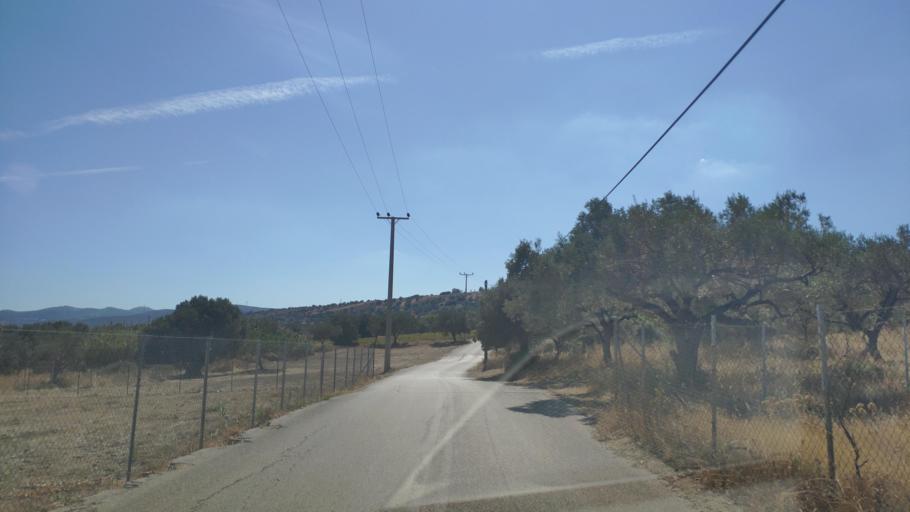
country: GR
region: Attica
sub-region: Nomarchia Anatolikis Attikis
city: Keratea
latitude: 37.8201
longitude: 23.9922
